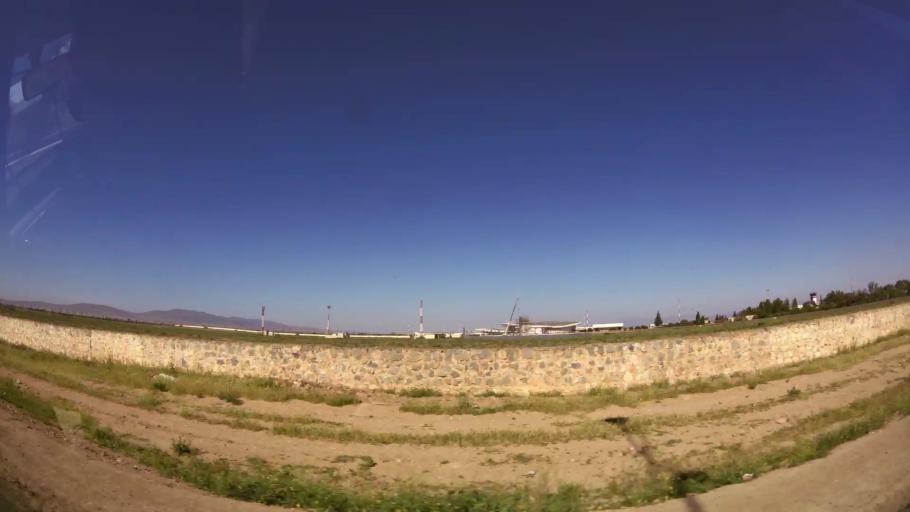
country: MA
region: Oriental
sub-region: Oujda-Angad
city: Oujda
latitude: 34.7855
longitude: -1.9490
